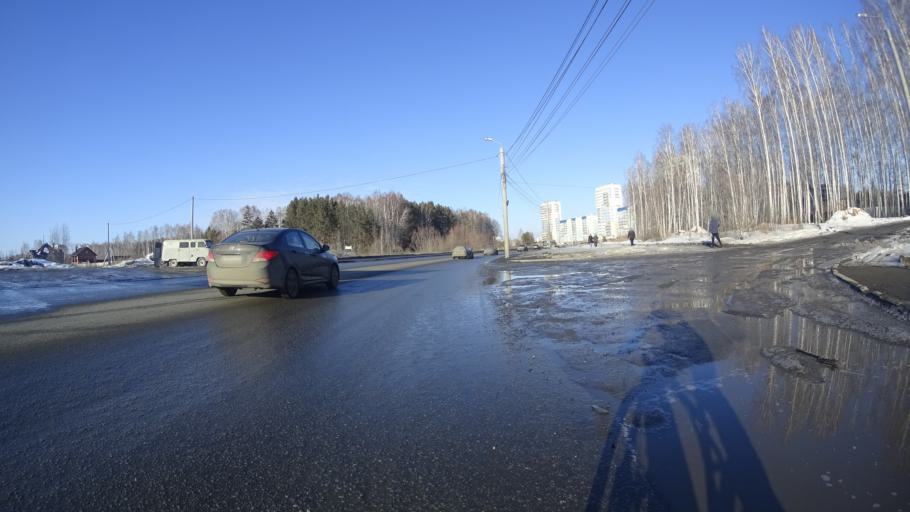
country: RU
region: Chelyabinsk
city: Roshchino
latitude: 55.1997
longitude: 61.2805
